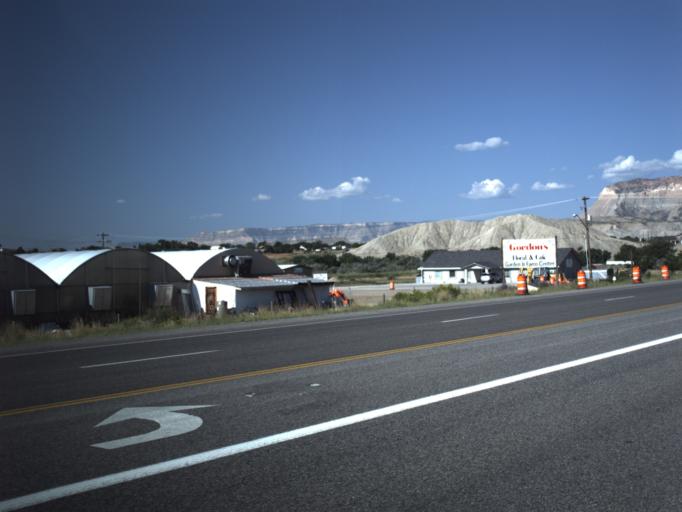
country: US
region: Utah
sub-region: Emery County
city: Huntington
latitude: 39.3394
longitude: -110.9554
